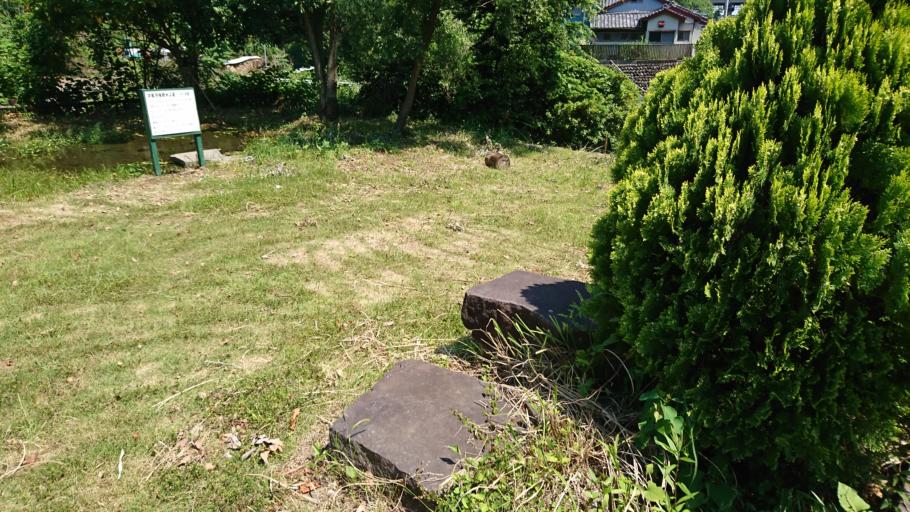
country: JP
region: Shizuoka
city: Fujinomiya
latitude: 35.1208
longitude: 138.5917
